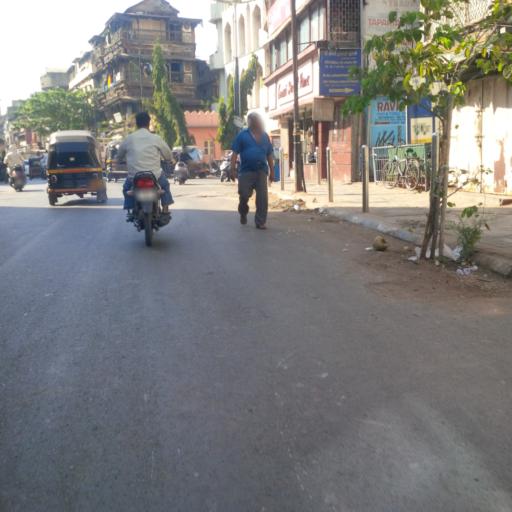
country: IN
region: Maharashtra
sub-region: Pune Division
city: Pune
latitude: 18.5160
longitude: 73.8604
